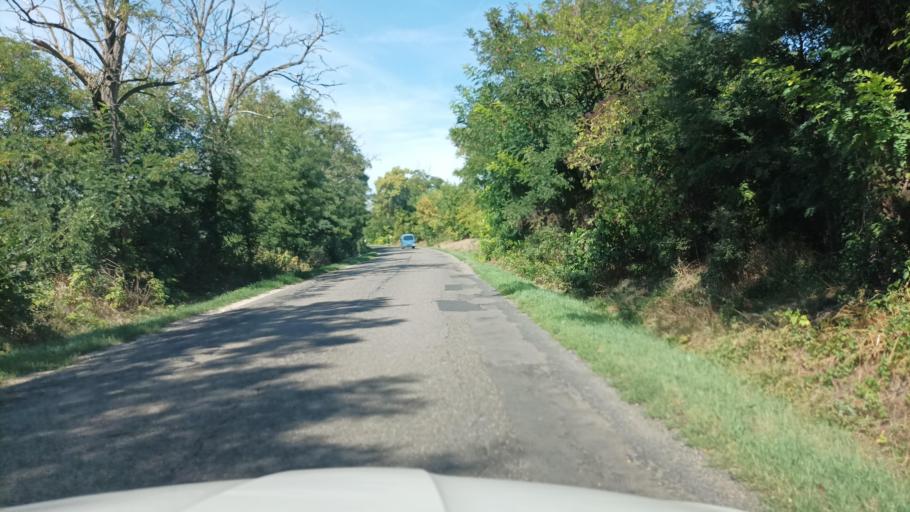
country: HU
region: Pest
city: Vacszentlaszlo
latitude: 47.5611
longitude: 19.5603
